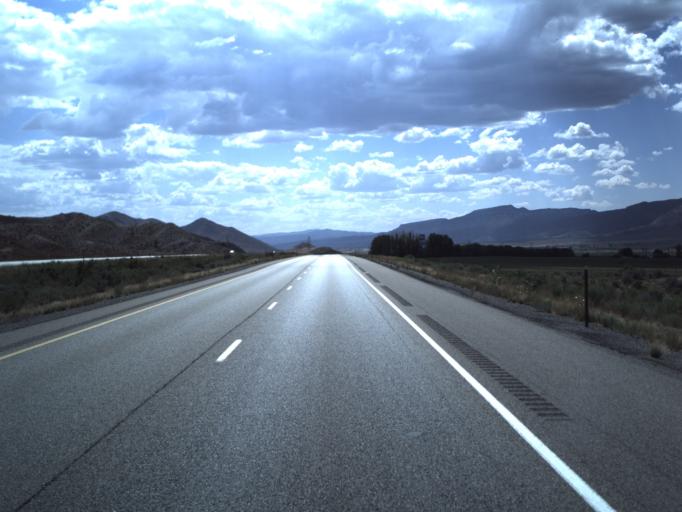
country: US
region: Utah
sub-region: Sevier County
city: Aurora
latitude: 38.9100
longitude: -111.8930
